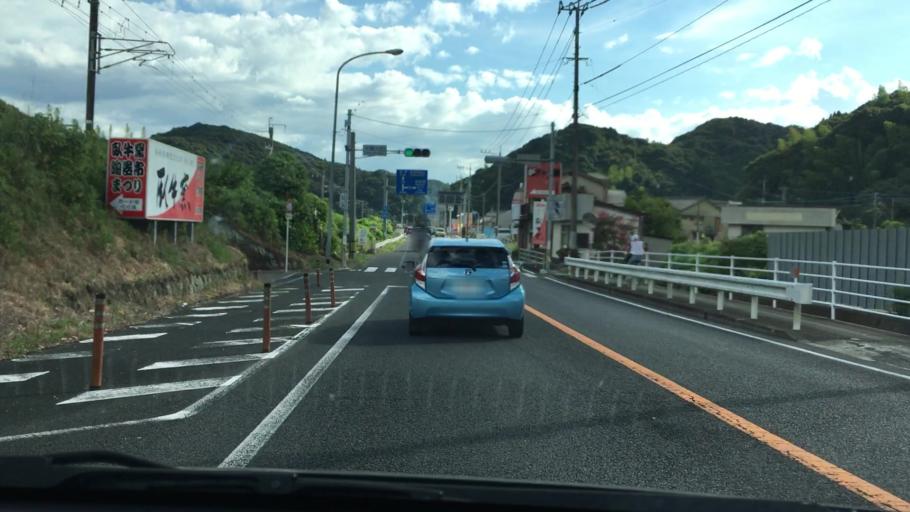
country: JP
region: Saga Prefecture
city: Imaricho-ko
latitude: 33.1690
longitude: 129.8427
